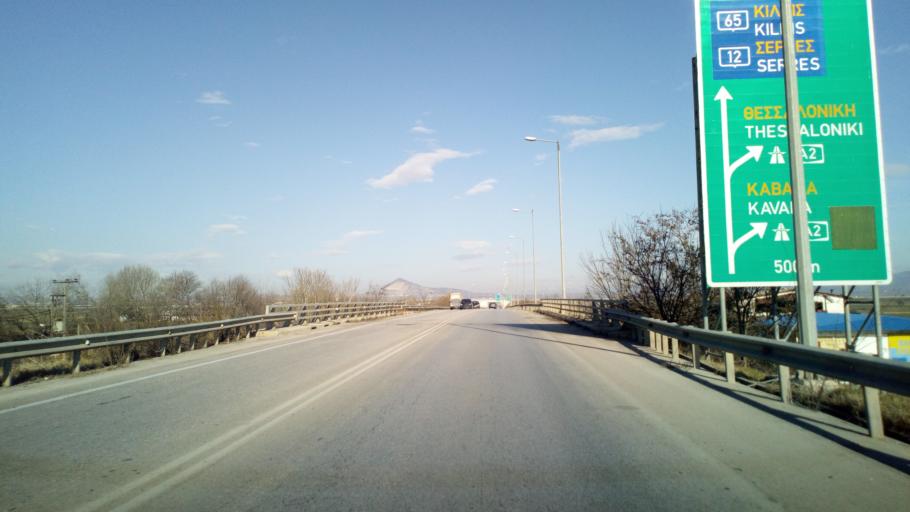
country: GR
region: Central Macedonia
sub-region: Nomos Thessalonikis
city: Lagyna
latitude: 40.7311
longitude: 23.0134
